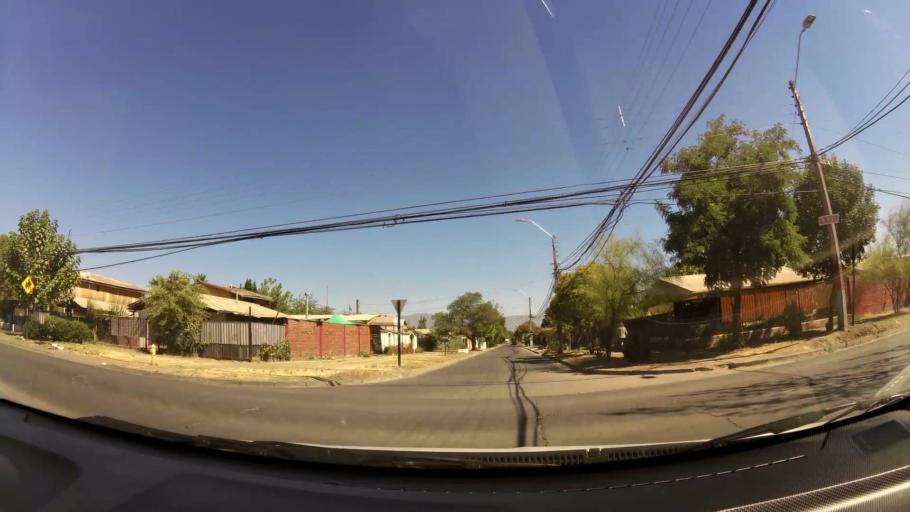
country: CL
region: O'Higgins
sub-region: Provincia de Cachapoal
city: Rancagua
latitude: -34.1674
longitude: -70.7058
